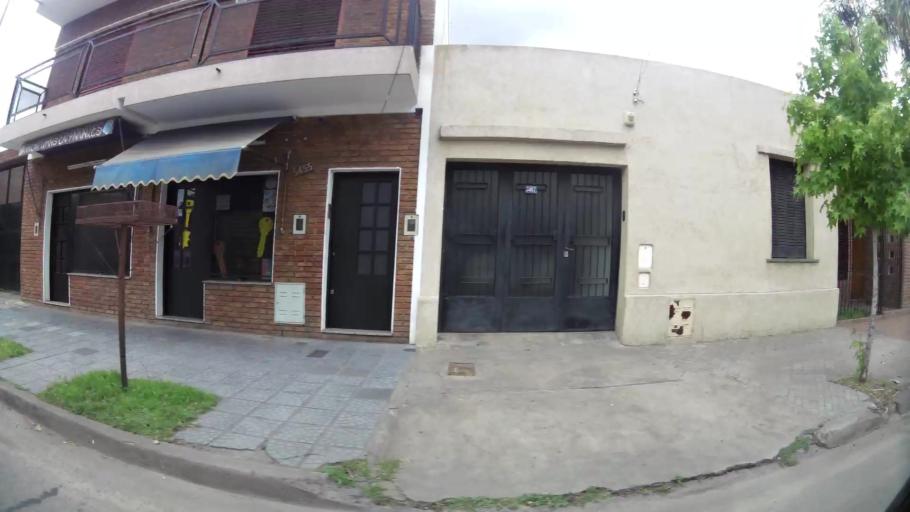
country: AR
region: Santa Fe
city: Gobernador Galvez
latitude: -33.0005
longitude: -60.6471
